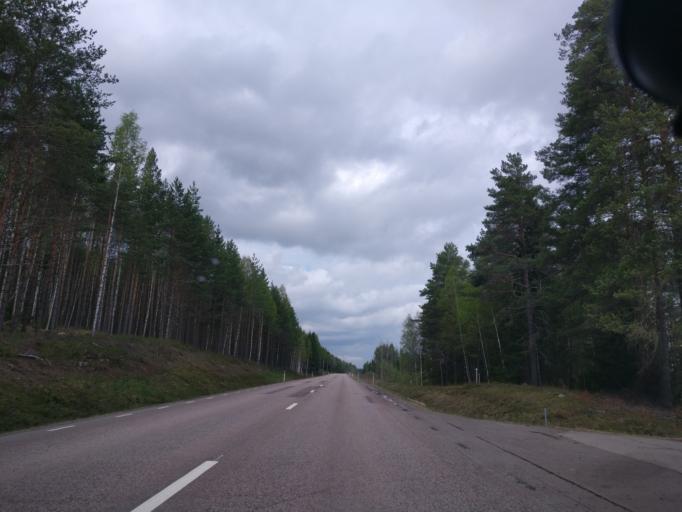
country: SE
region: Vaermland
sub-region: Hagfors Kommun
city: Ekshaerad
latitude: 60.1456
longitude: 13.5230
